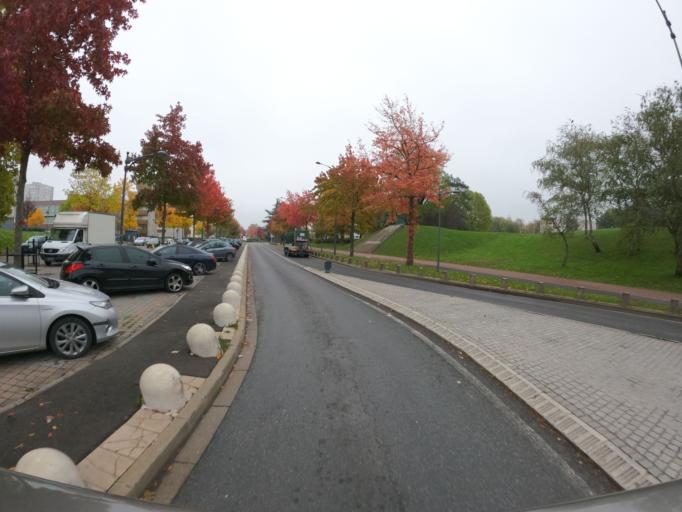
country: FR
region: Ile-de-France
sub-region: Departement du Val-de-Marne
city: Chennevieres-sur-Marne
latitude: 48.8041
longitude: 2.5527
